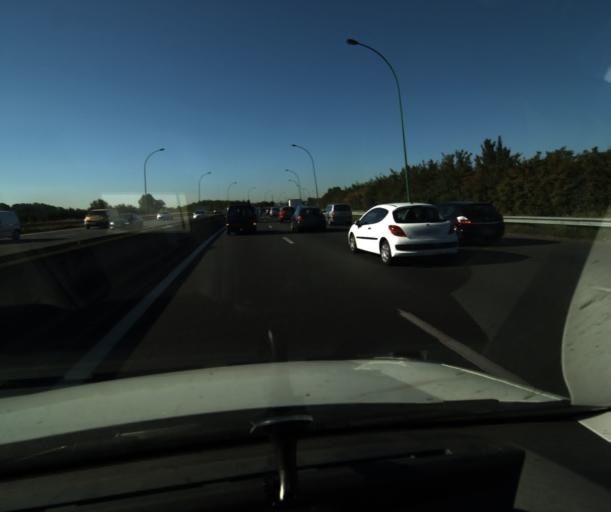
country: FR
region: Midi-Pyrenees
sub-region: Departement de la Haute-Garonne
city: Balma
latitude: 43.5806
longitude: 1.4982
